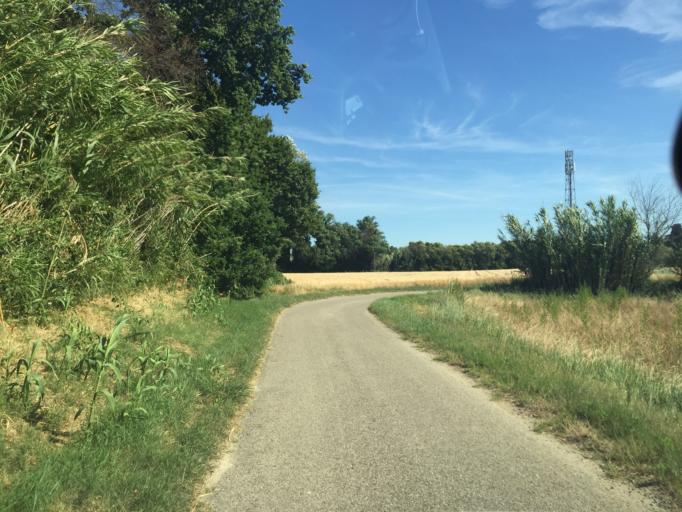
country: FR
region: Languedoc-Roussillon
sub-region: Departement du Gard
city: Montfaucon
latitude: 44.0867
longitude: 4.7649
